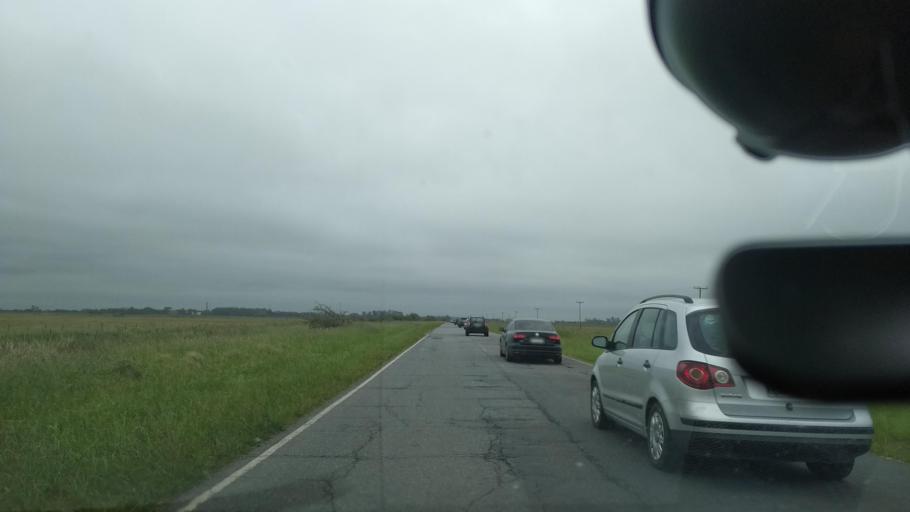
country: AR
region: Buenos Aires
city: Veronica
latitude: -35.5541
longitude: -57.3070
